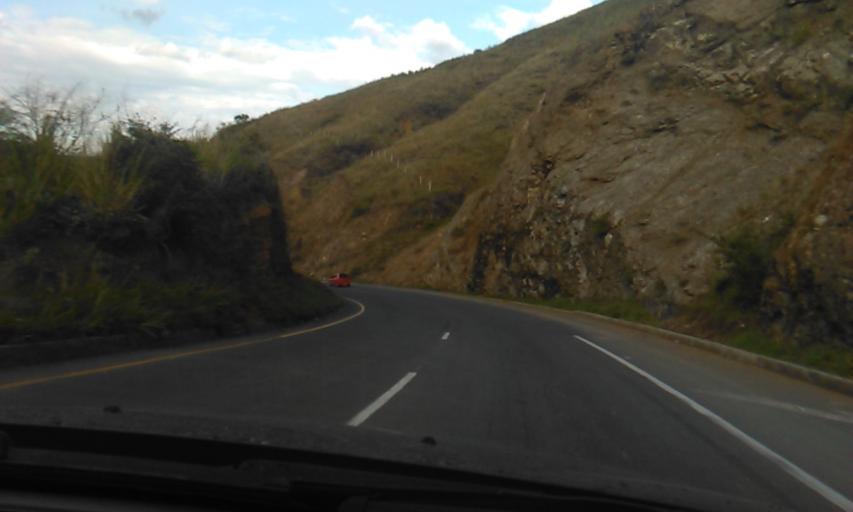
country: CO
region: Valle del Cauca
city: Yotoco
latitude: 3.8932
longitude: -76.3892
